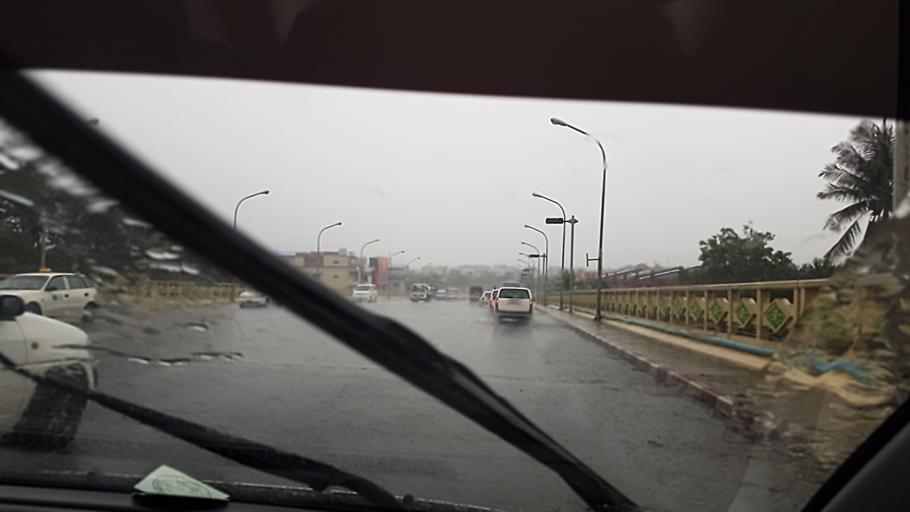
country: MM
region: Yangon
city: Yangon
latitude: 16.7796
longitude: 96.1846
